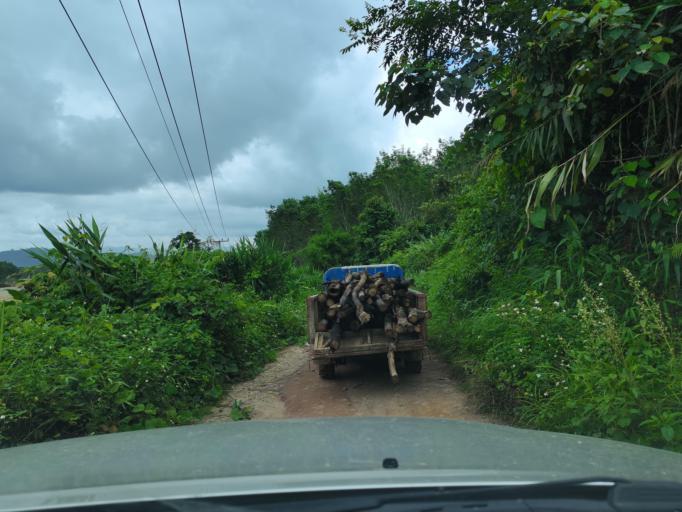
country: LA
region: Loungnamtha
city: Muang Long
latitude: 20.7012
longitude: 101.0348
